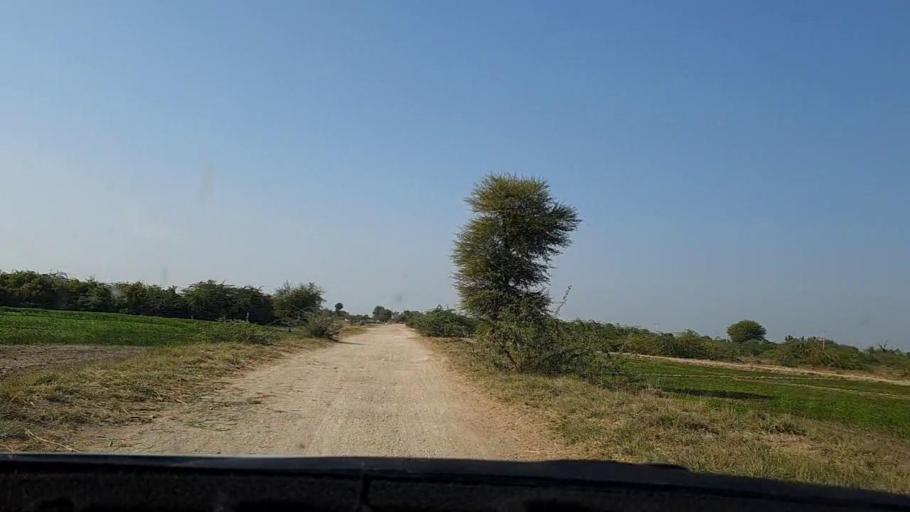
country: PK
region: Sindh
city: Tando Mittha Khan
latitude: 25.8132
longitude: 69.2913
